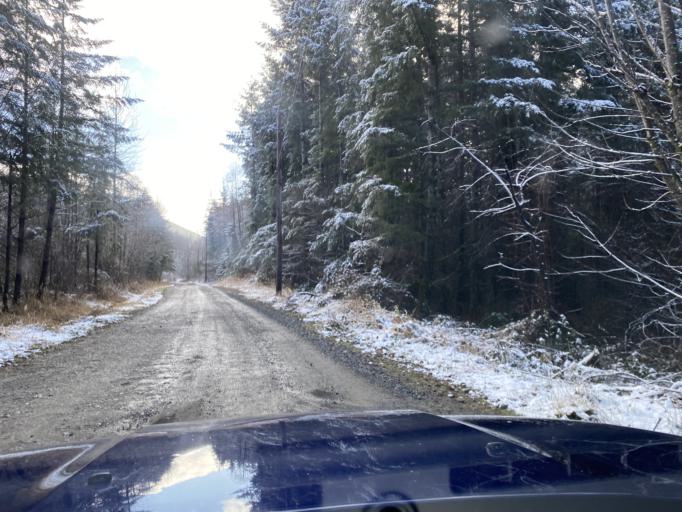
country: US
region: Washington
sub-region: King County
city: Snoqualmie
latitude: 47.4981
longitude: -121.8758
